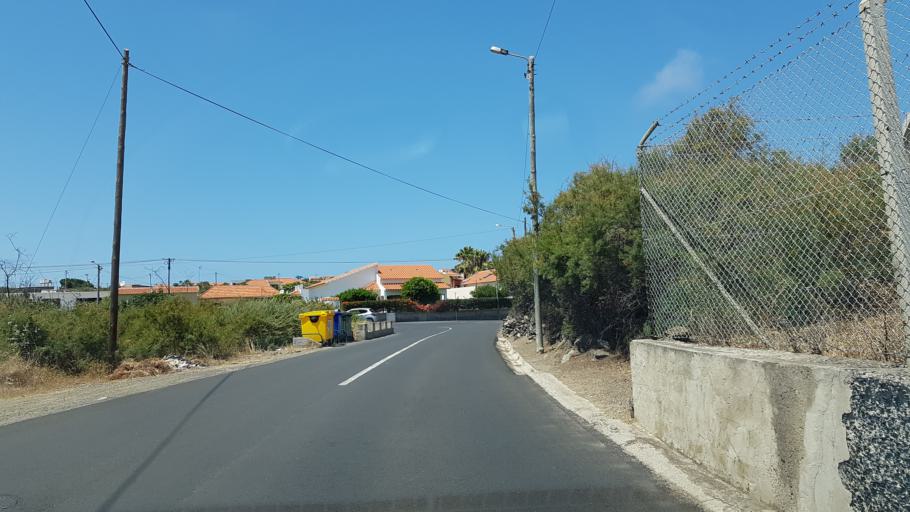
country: PT
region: Madeira
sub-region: Porto Santo
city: Camacha
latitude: 33.0778
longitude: -16.3464
